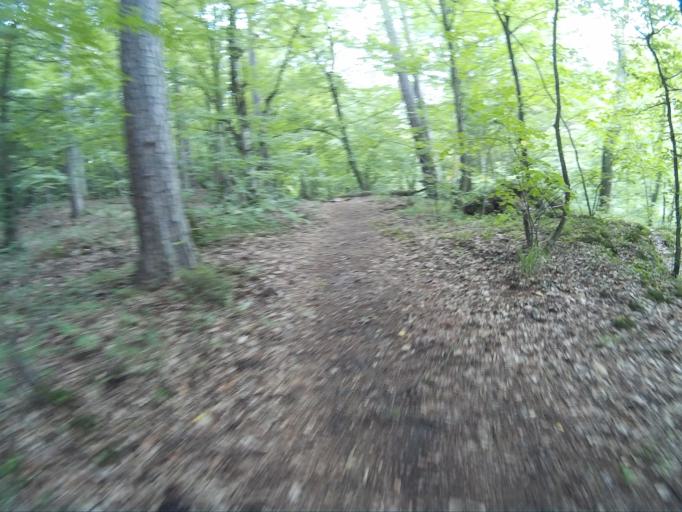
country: PL
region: Kujawsko-Pomorskie
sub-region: Powiat tucholski
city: Tuchola
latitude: 53.5321
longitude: 17.8778
